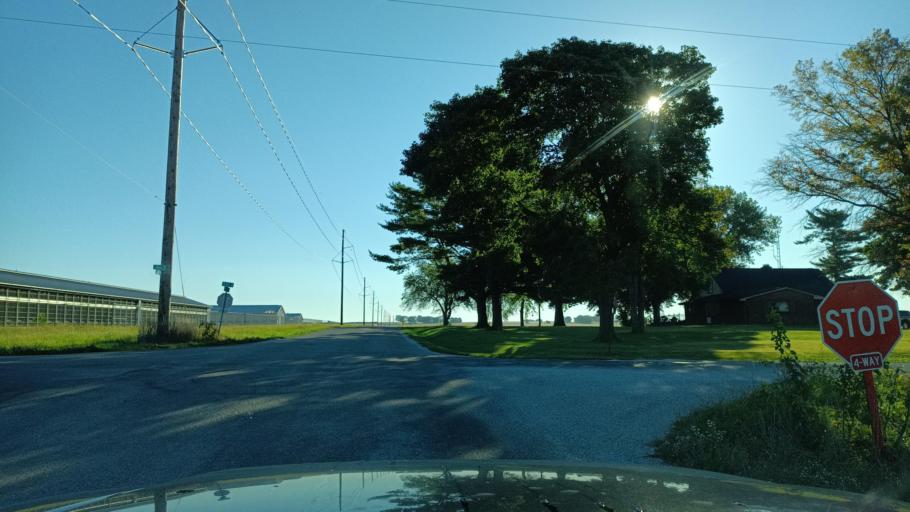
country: US
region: Illinois
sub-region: Champaign County
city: Savoy
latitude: 40.0546
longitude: -88.2095
